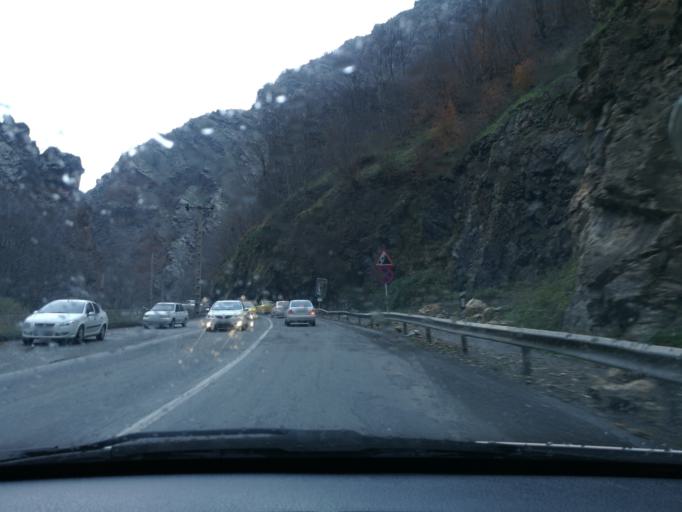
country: IR
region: Mazandaran
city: Chalus
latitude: 36.2760
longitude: 51.2442
